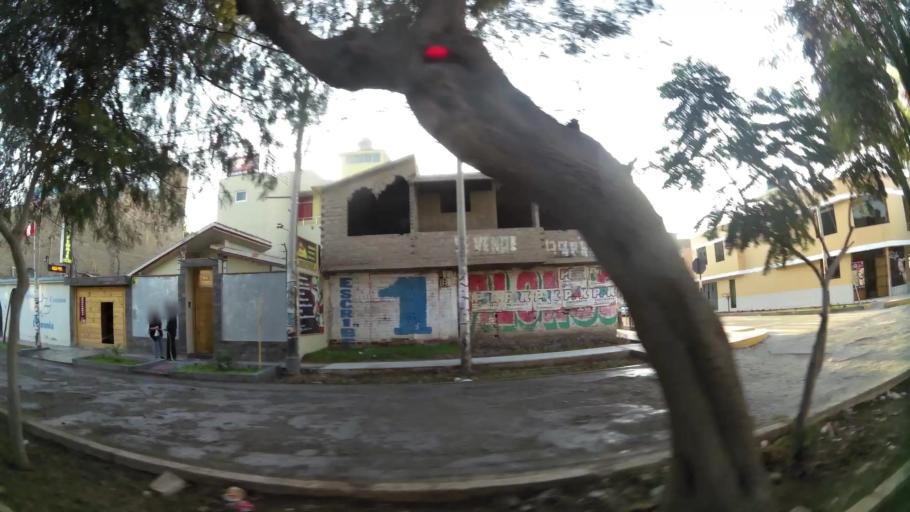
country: PE
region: Ica
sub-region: Provincia de Ica
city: Ica
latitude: -14.0836
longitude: -75.7266
